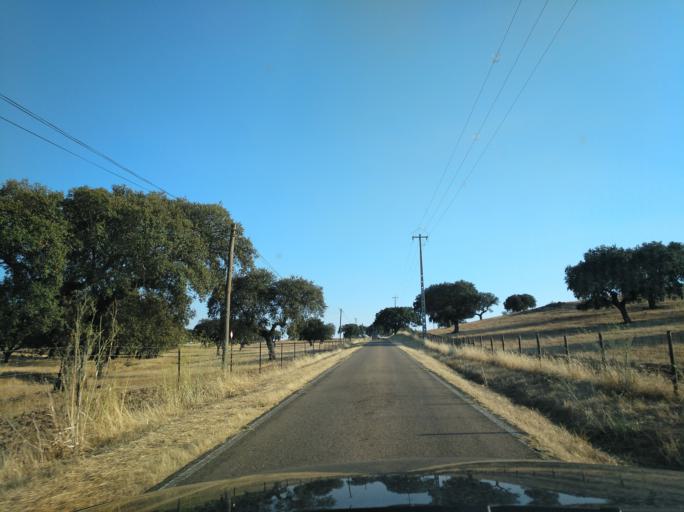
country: PT
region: Portalegre
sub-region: Campo Maior
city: Campo Maior
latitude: 39.0733
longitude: -7.1153
